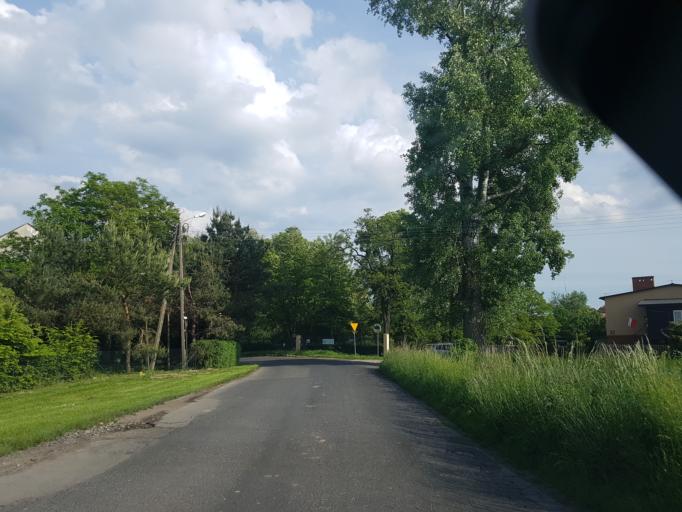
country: PL
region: Lower Silesian Voivodeship
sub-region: Powiat strzelinski
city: Wiazow
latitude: 50.8557
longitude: 17.1833
